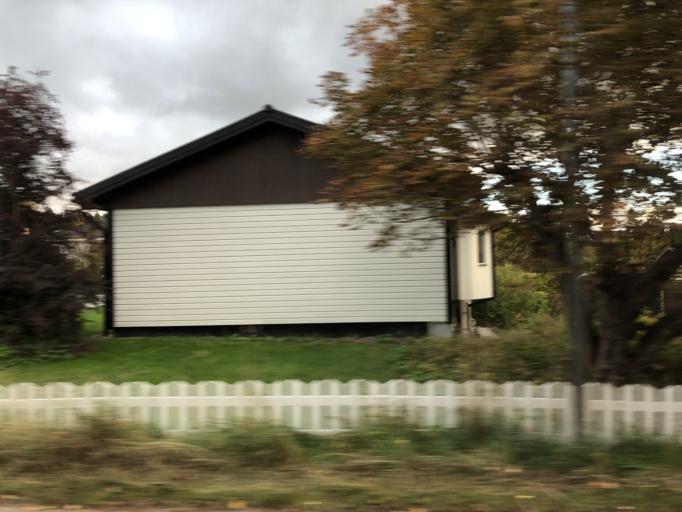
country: SE
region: Stockholm
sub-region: Jarfalla Kommun
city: Jakobsberg
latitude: 59.4239
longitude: 17.8083
